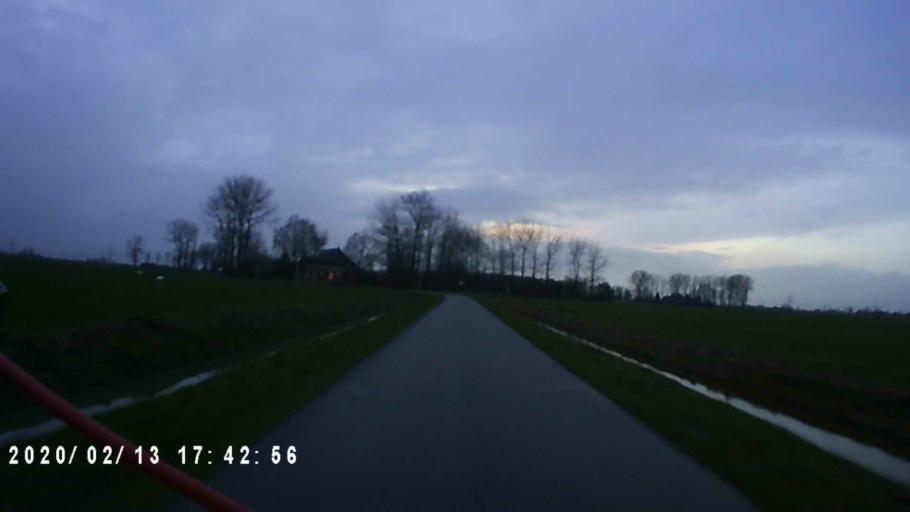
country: NL
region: Groningen
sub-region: Gemeente Zuidhorn
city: Aduard
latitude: 53.2304
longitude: 6.4878
